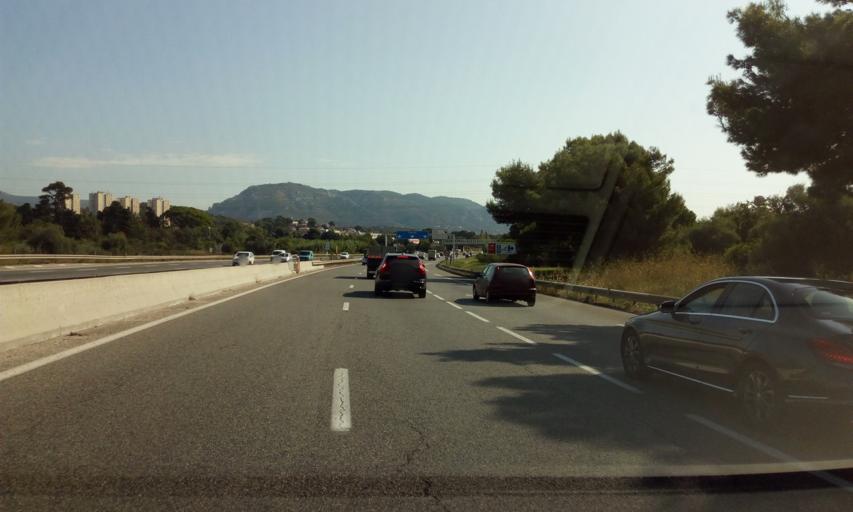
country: FR
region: Provence-Alpes-Cote d'Azur
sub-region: Departement du Var
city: Ollioules
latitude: 43.1245
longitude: 5.8728
